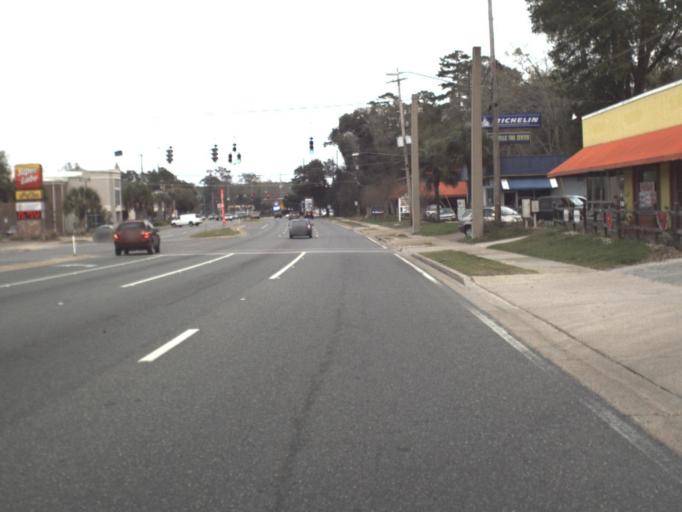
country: US
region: Florida
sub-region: Leon County
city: Tallahassee
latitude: 30.4645
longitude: -84.2701
